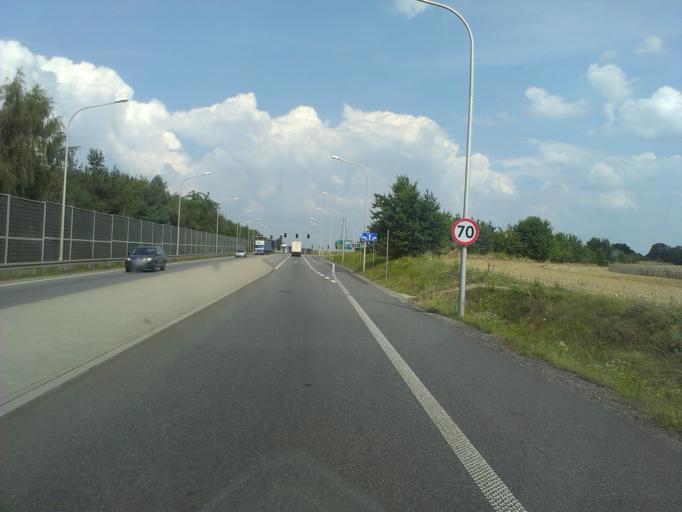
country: PL
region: Lower Silesian Voivodeship
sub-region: Powiat sredzki
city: Sroda Slaska
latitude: 51.1593
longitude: 16.6040
